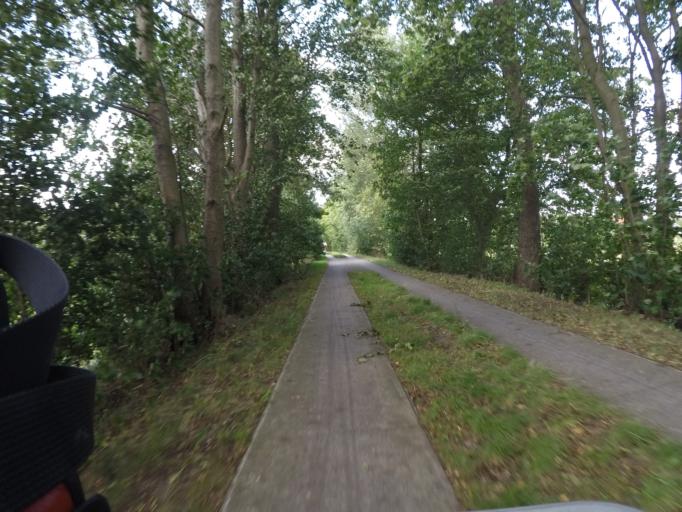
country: DE
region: Lower Saxony
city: Stelle
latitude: 53.4410
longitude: 10.1352
